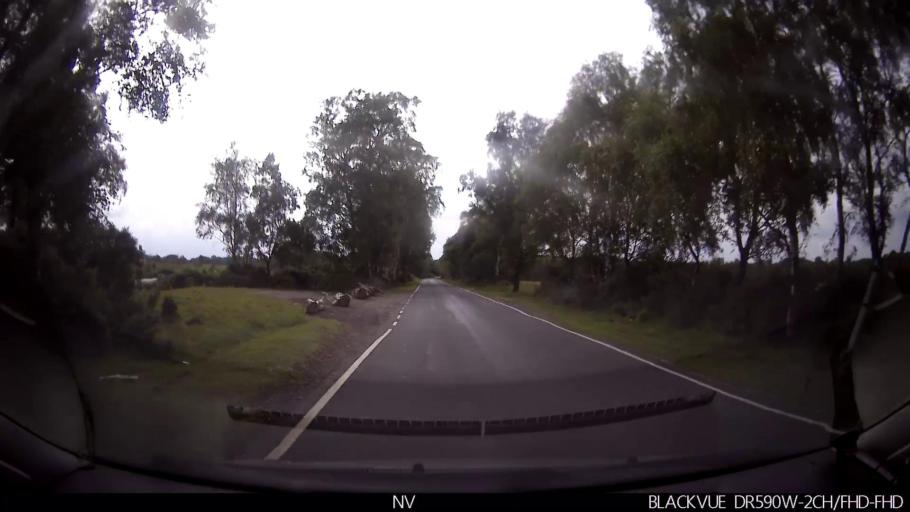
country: GB
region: England
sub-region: North Yorkshire
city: Strensall
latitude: 54.0473
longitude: -0.9988
